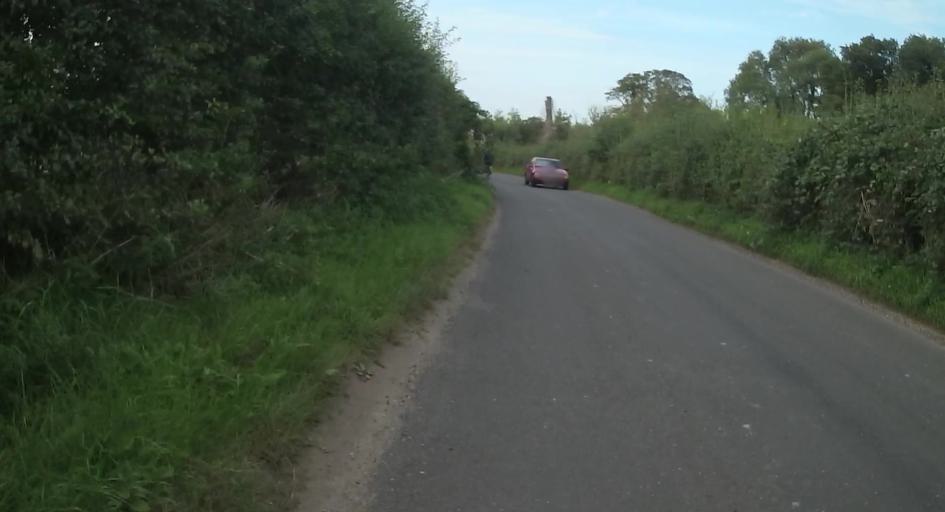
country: GB
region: England
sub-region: Hampshire
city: Kings Worthy
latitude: 51.0749
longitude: -1.1833
